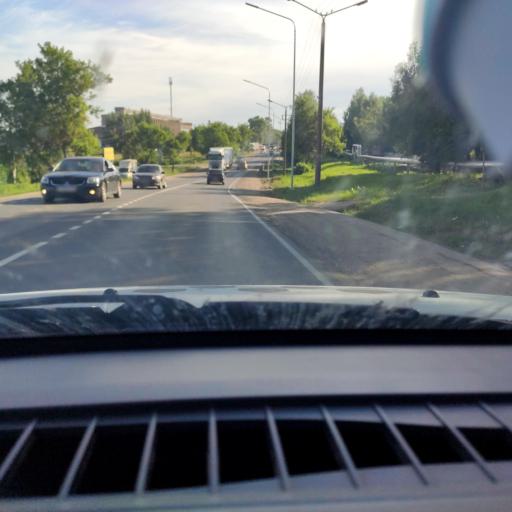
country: RU
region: Kirov
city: Vakhrushi
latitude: 58.6856
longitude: 50.0367
